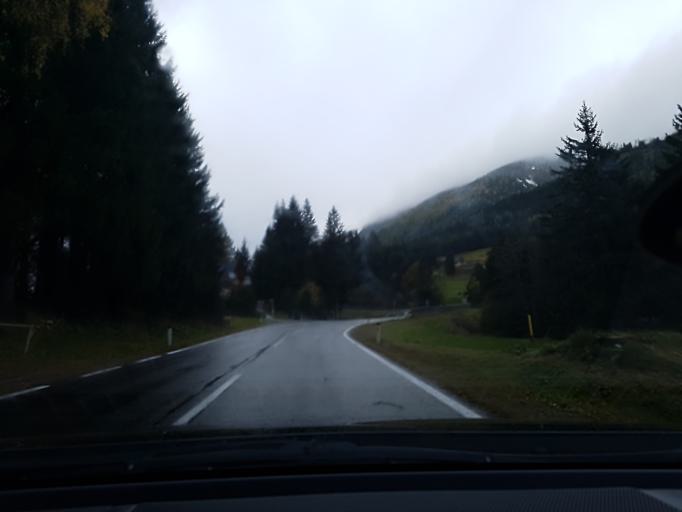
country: AT
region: Styria
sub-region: Politischer Bezirk Murtal
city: Hohentauern
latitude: 47.3941
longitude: 14.4643
